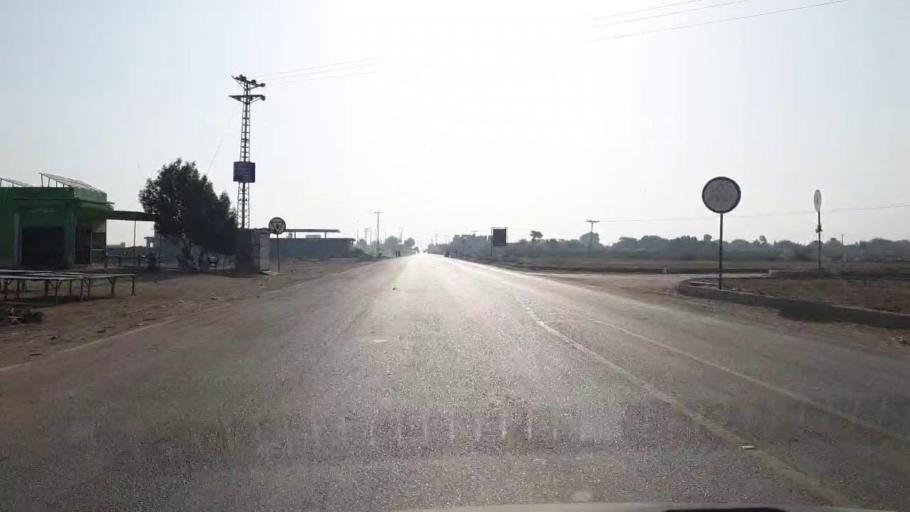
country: PK
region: Sindh
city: Badin
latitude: 24.6776
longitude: 68.8462
